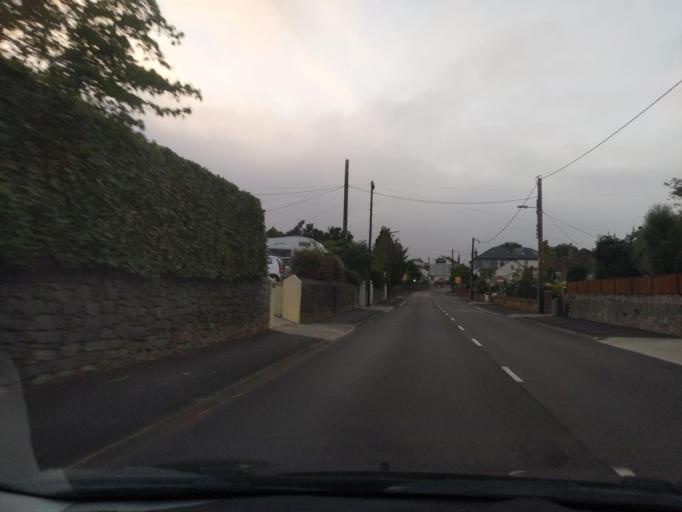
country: GB
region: England
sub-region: Borough of Torbay
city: Paignton
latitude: 50.4438
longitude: -3.5827
